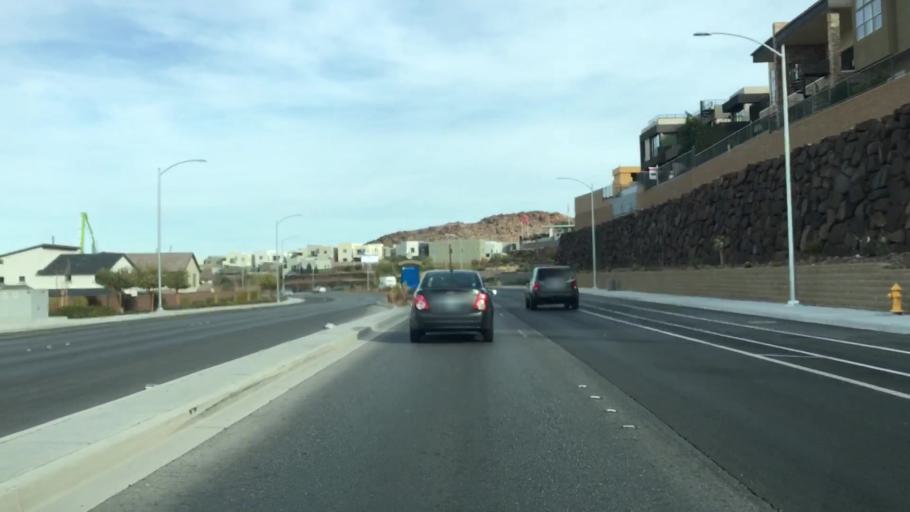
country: US
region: Nevada
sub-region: Clark County
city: Whitney
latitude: 35.9979
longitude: -115.0865
